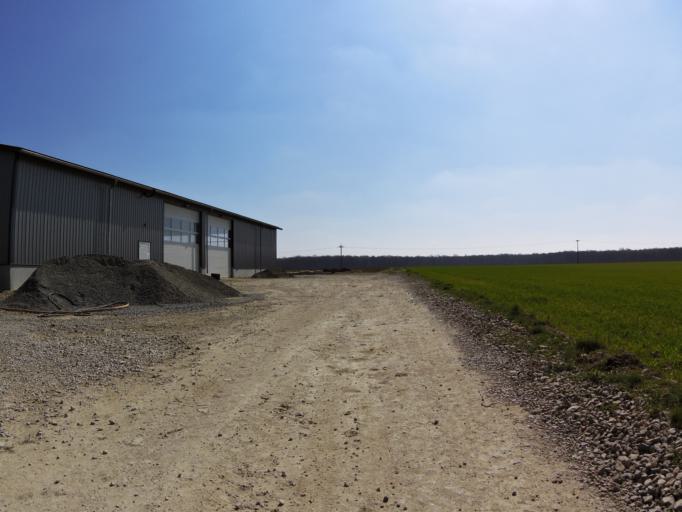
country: DE
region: Bavaria
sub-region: Regierungsbezirk Unterfranken
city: Biebelried
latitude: 49.7297
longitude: 10.0954
